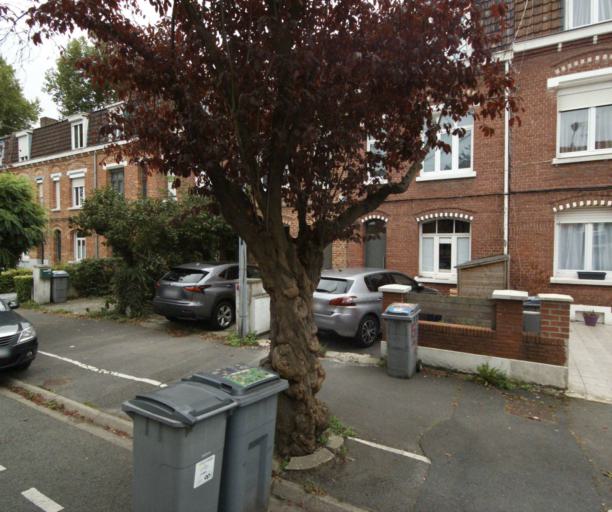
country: FR
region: Nord-Pas-de-Calais
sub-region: Departement du Nord
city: Lambersart
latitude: 50.6452
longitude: 3.0337
